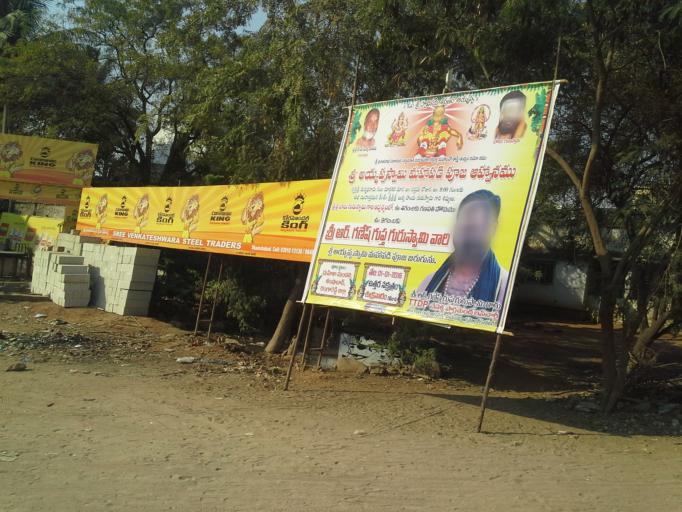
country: IN
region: Telangana
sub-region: Rangareddi
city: Balapur
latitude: 17.2613
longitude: 78.3872
